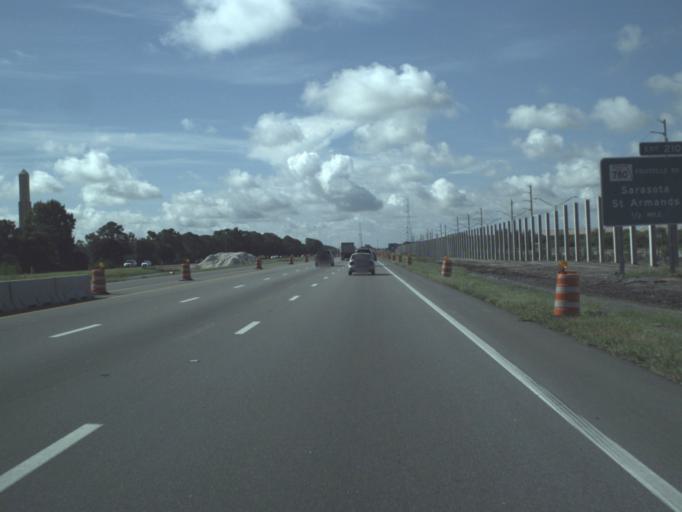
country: US
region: Florida
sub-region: Sarasota County
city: The Meadows
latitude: 27.3546
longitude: -82.4468
